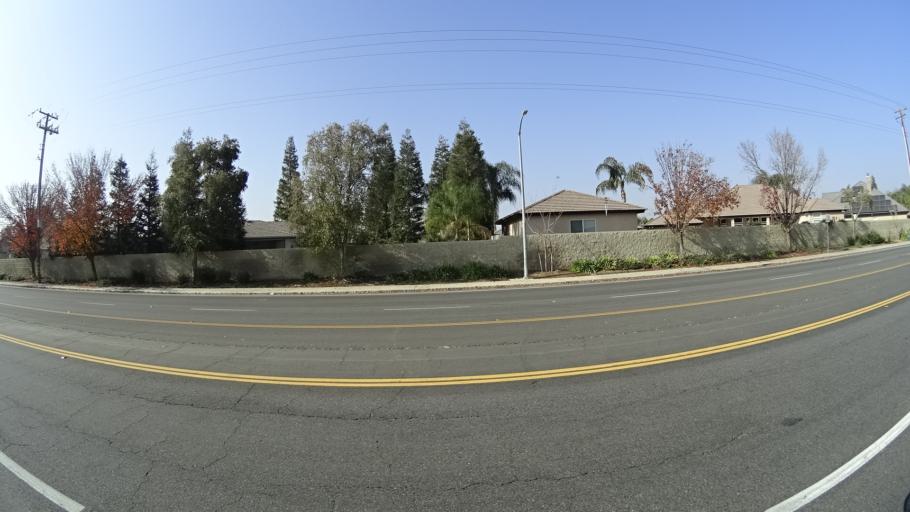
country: US
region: California
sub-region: Kern County
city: Rosedale
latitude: 35.4151
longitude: -119.1278
